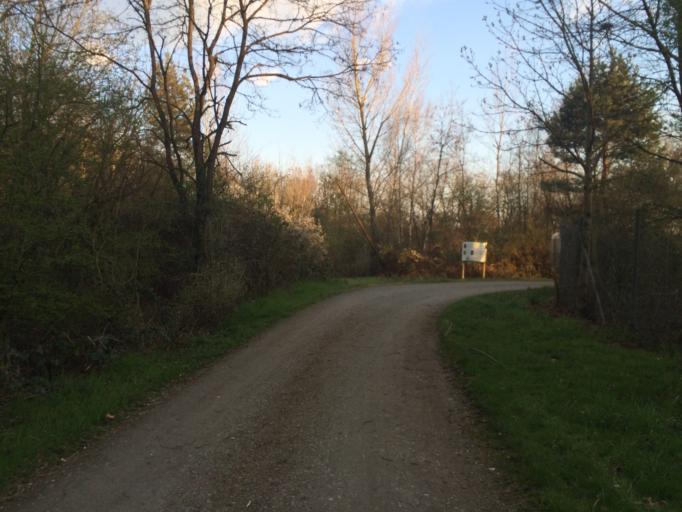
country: DE
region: Hesse
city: Morfelden-Walldorf
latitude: 49.9864
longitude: 8.5945
